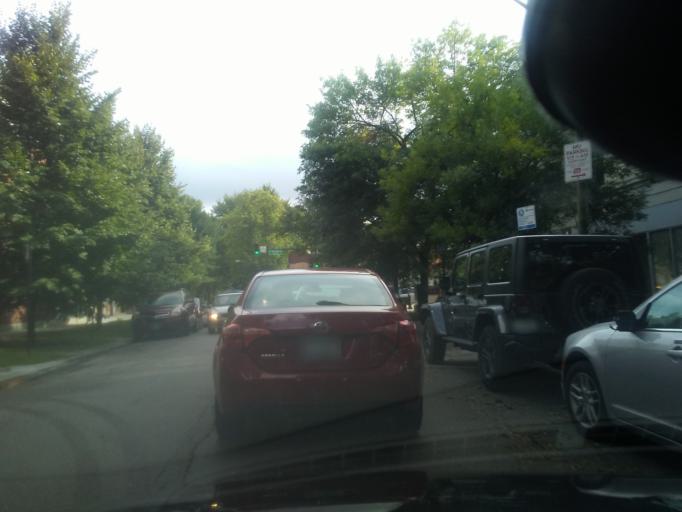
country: US
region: Illinois
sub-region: Cook County
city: Evanston
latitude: 41.9986
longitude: -87.6656
